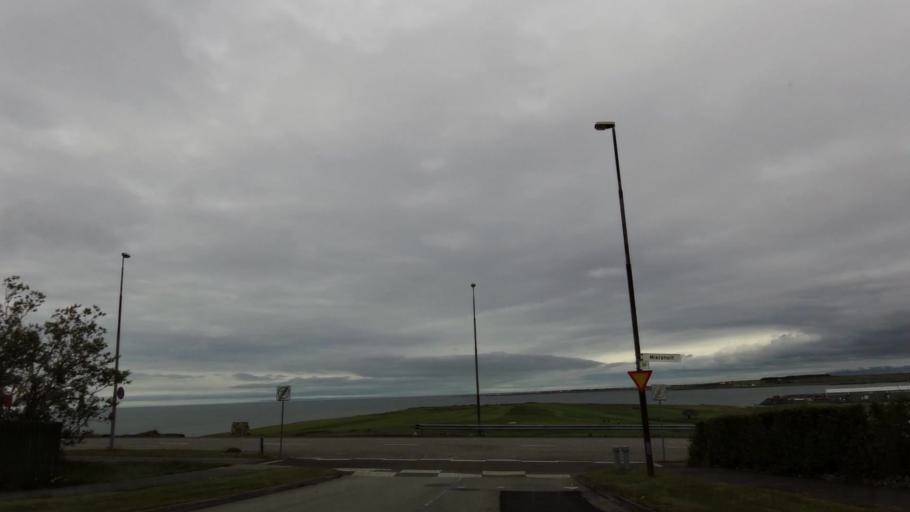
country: IS
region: Capital Region
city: Alftanes
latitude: 64.0592
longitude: -21.9884
